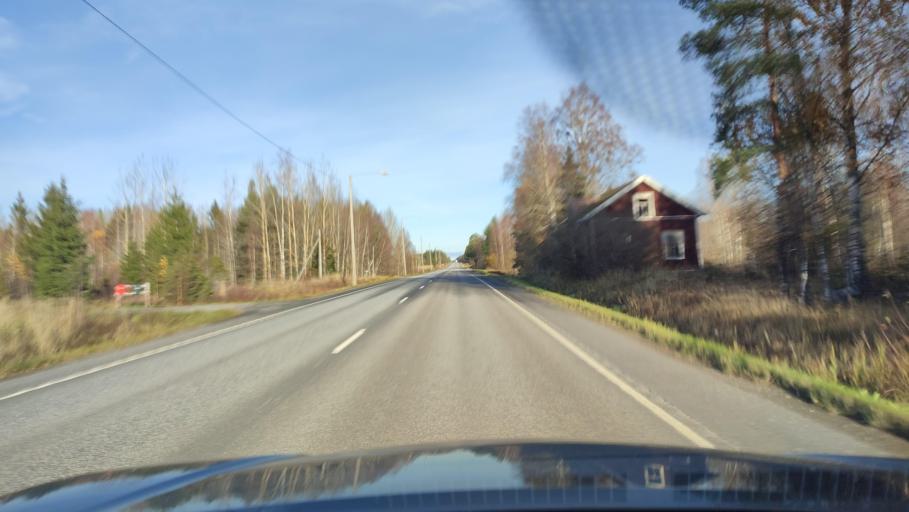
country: FI
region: Ostrobothnia
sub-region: Vaasa
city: Malax
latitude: 62.7789
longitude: 21.6634
